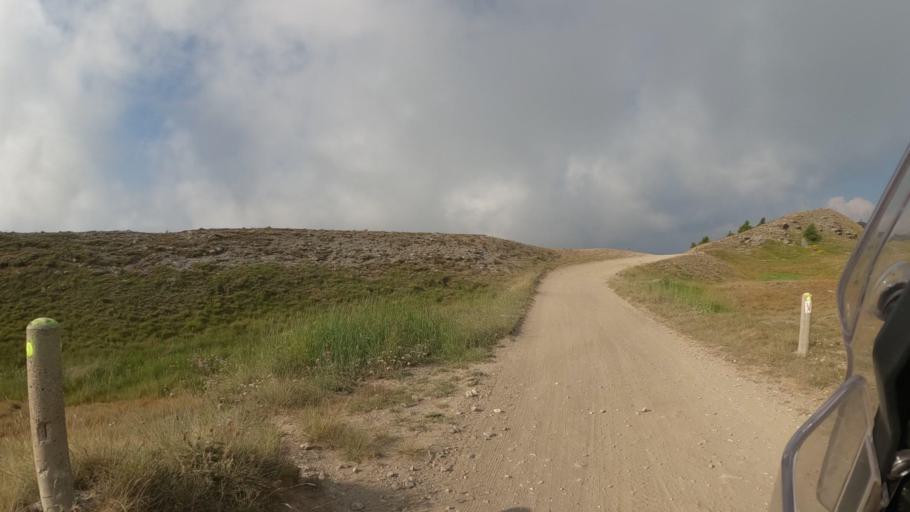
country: IT
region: Piedmont
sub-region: Provincia di Torino
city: Pragelato-Rua
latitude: 45.0325
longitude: 6.9091
